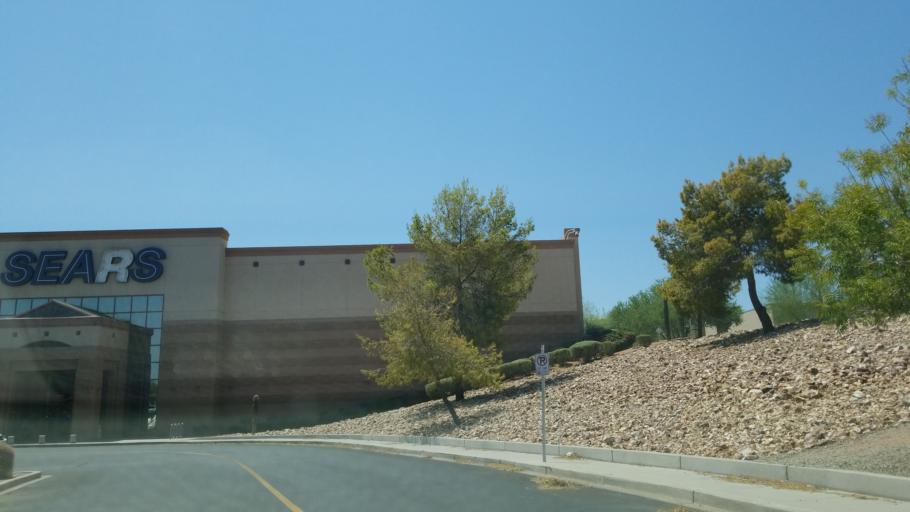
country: US
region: Arizona
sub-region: Maricopa County
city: Peoria
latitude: 33.6434
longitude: -112.2271
